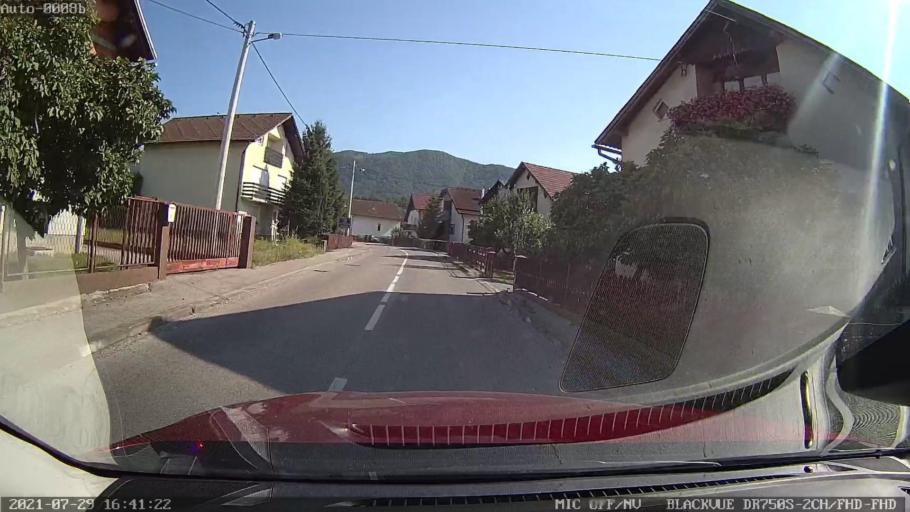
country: HR
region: Varazdinska
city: Ivanec
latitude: 46.2246
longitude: 16.1099
